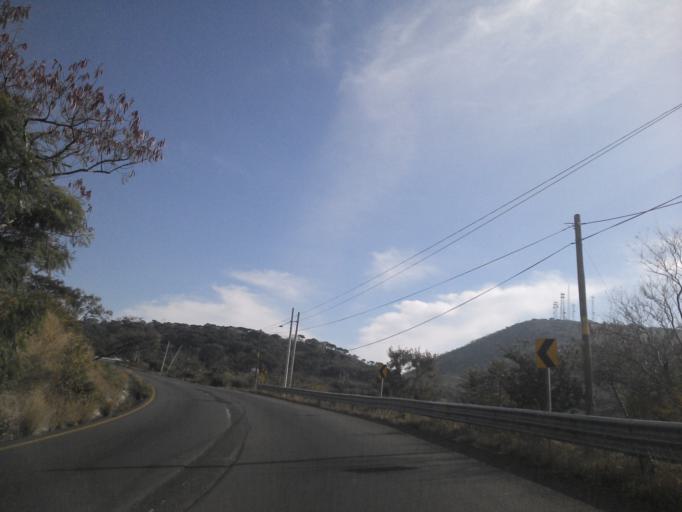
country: MX
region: Jalisco
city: Ixtlahuacan de los Membrillos
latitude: 20.3427
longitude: -103.1875
